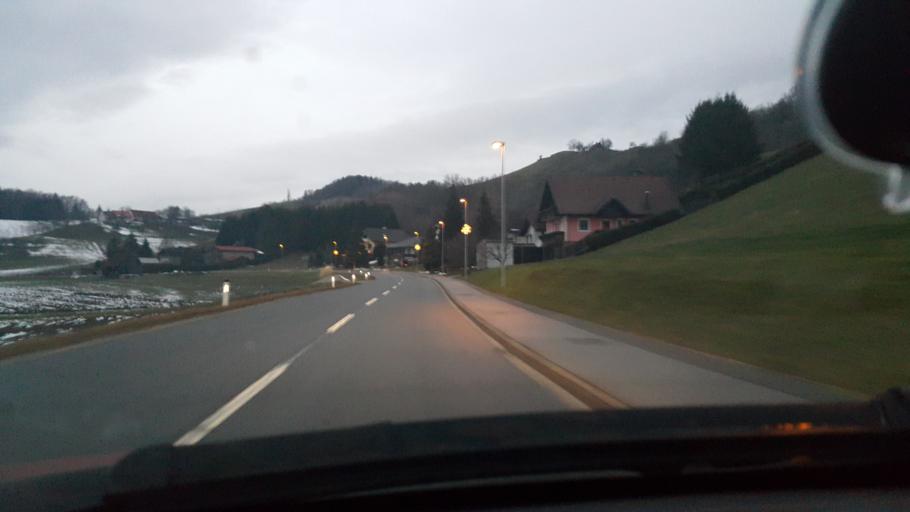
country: AT
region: Styria
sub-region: Politischer Bezirk Leibnitz
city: Sulztal an der Weinstrasse
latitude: 46.6460
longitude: 15.5658
